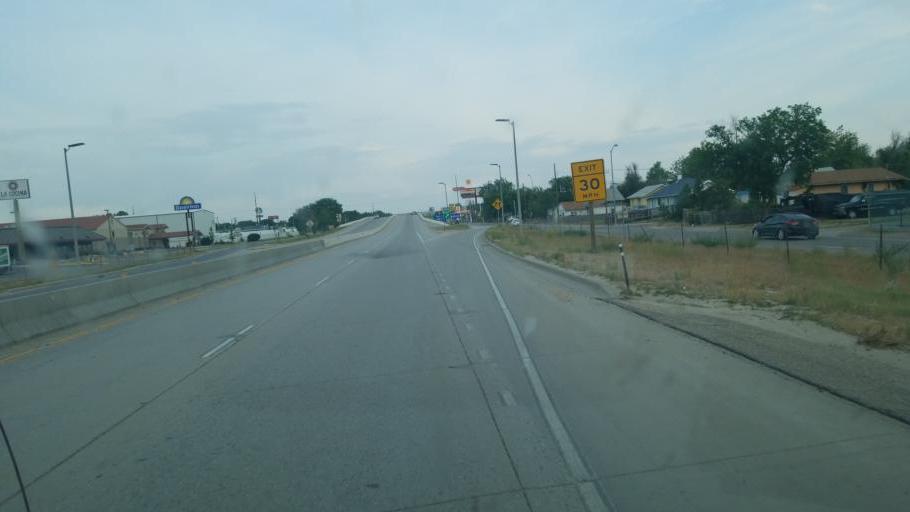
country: US
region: Wyoming
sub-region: Natrona County
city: Casper
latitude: 42.8571
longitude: -106.3201
